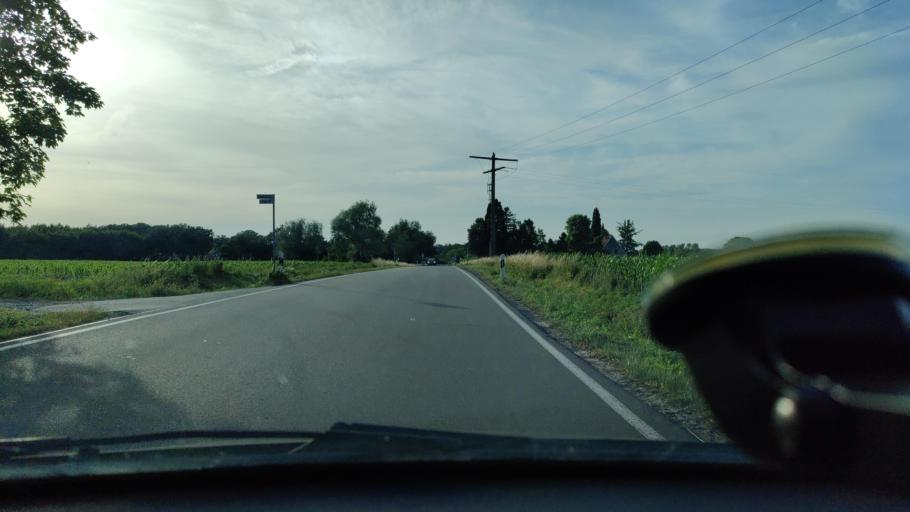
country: DE
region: North Rhine-Westphalia
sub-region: Regierungsbezirk Munster
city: Billerbeck
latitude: 51.9892
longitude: 7.2510
